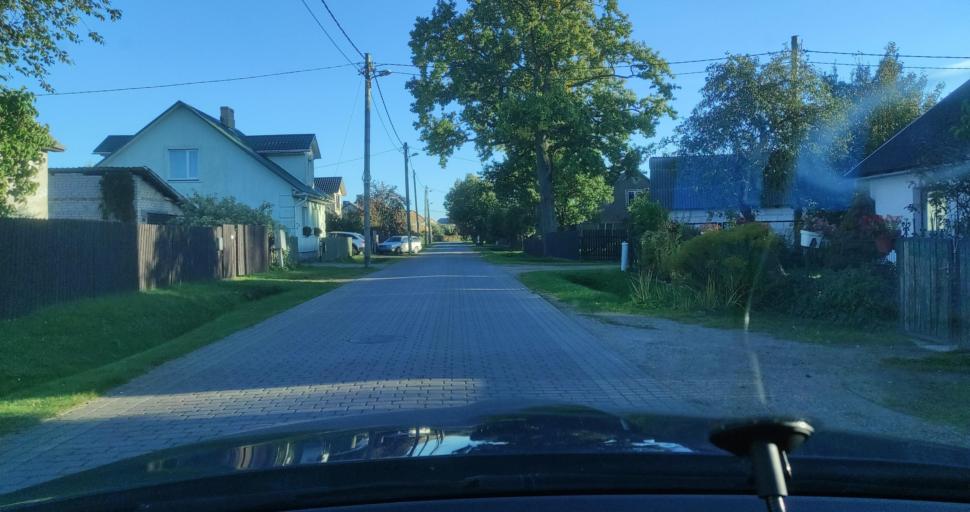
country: LV
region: Ventspils
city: Ventspils
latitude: 57.3751
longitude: 21.5767
